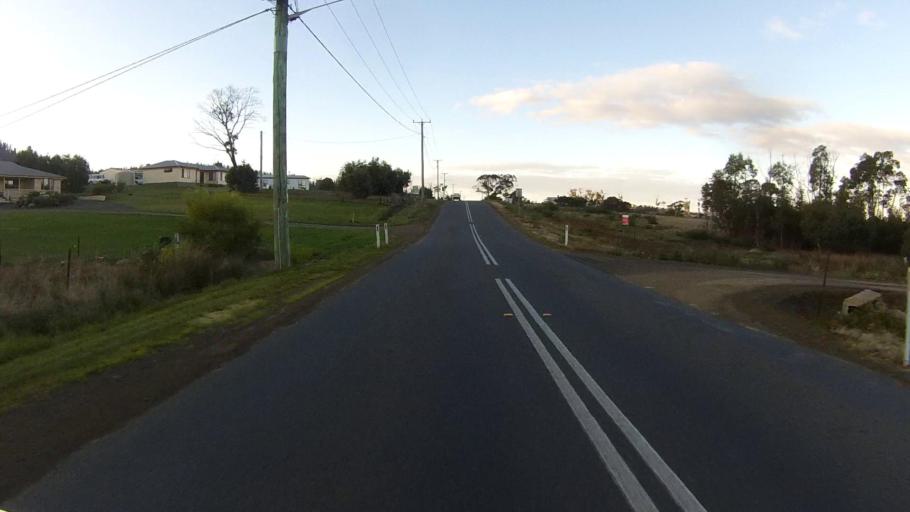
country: AU
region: Tasmania
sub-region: Sorell
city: Sorell
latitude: -42.8827
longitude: 147.8162
